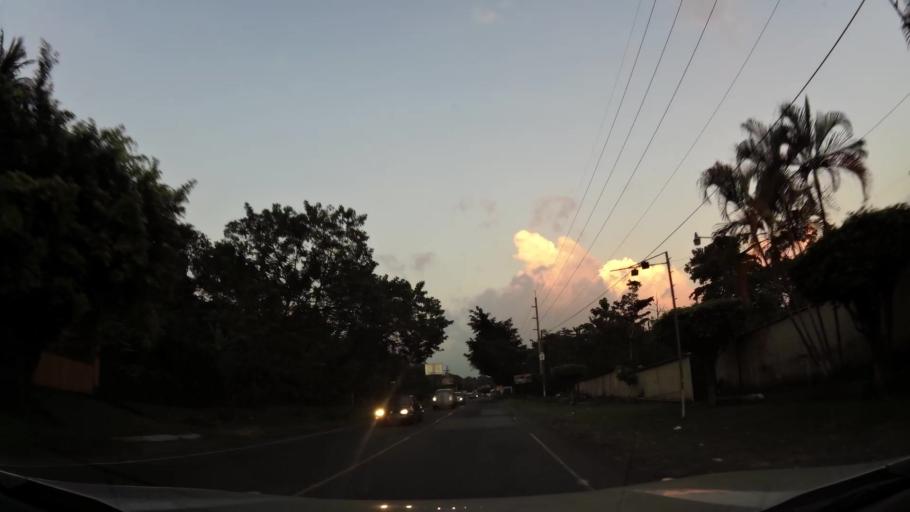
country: GT
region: Retalhuleu
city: Santa Cruz Mulua
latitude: 14.5844
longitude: -91.6243
